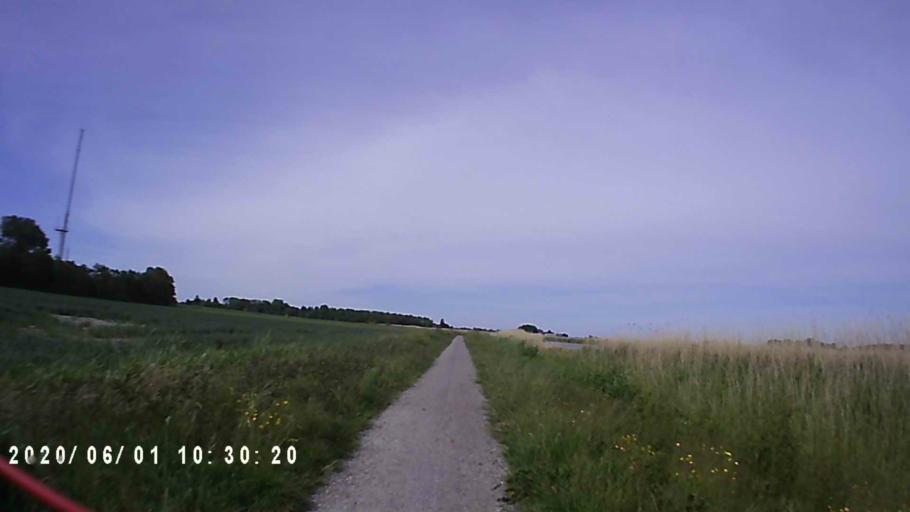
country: NL
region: Friesland
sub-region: Gemeente Het Bildt
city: Minnertsga
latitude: 53.2305
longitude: 5.6023
